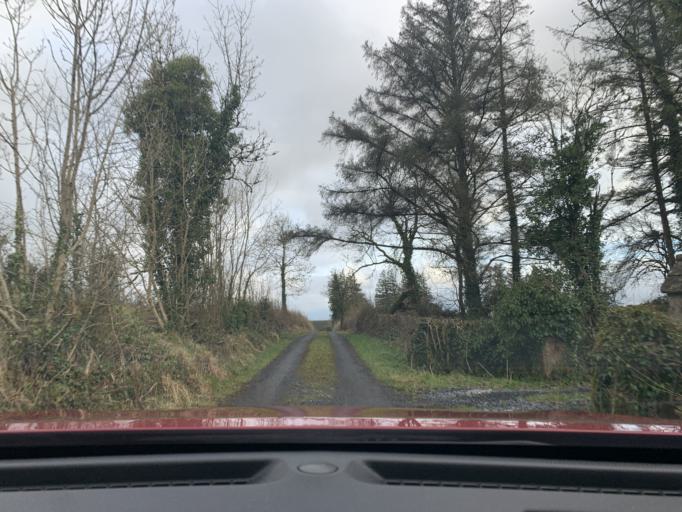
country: IE
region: Connaught
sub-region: Sligo
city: Ballymote
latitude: 54.0236
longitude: -8.5122
